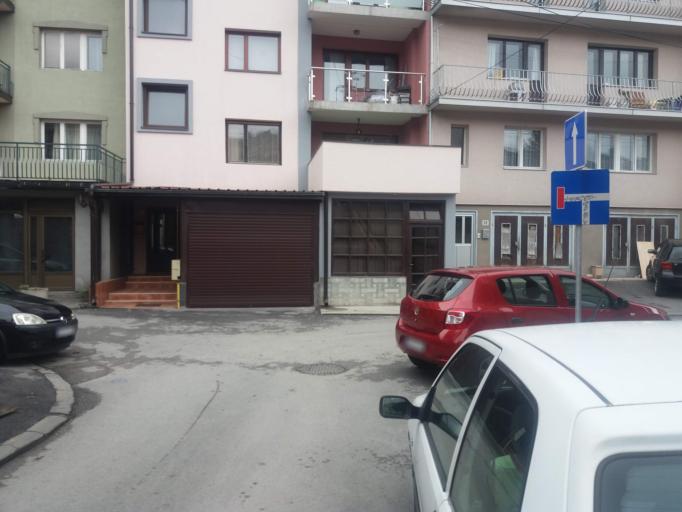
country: RS
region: Central Serbia
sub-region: Zlatiborski Okrug
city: Uzice
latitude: 43.8582
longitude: 19.8487
